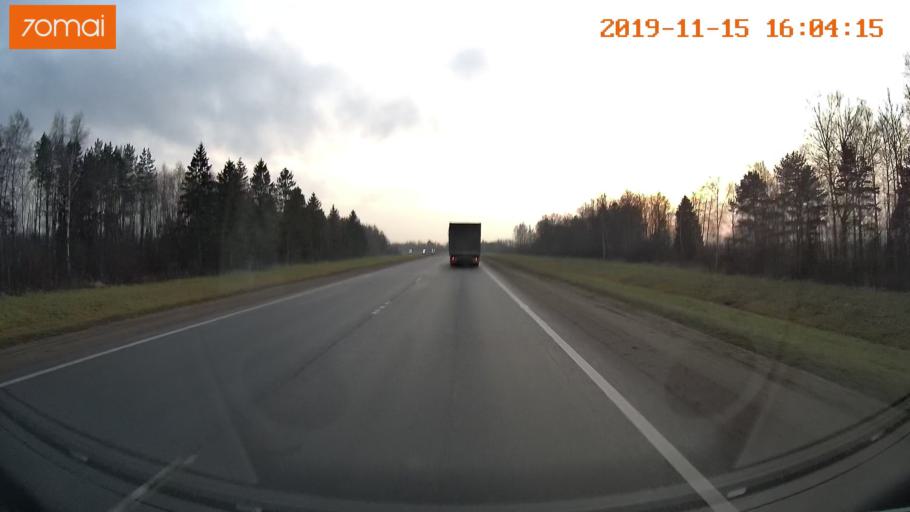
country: RU
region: Jaroslavl
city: Yaroslavl
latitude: 57.7499
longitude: 39.9040
